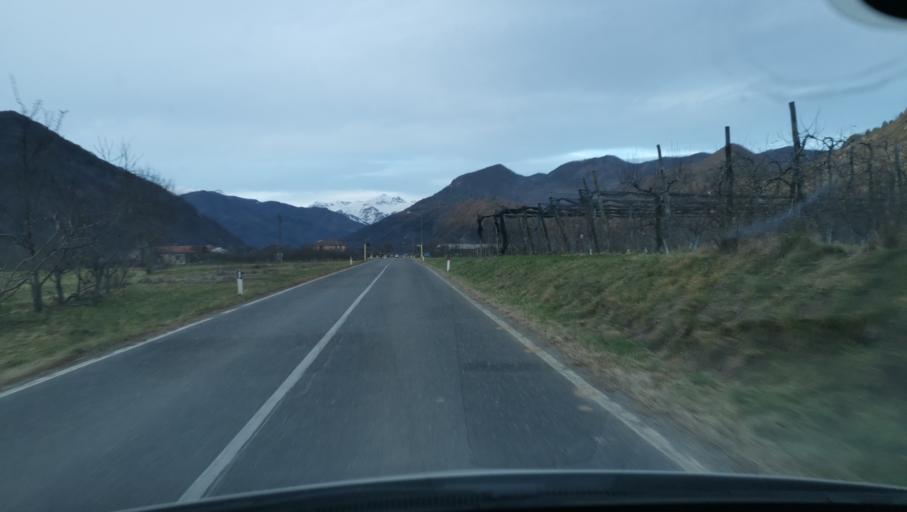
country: IT
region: Piedmont
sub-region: Provincia di Cuneo
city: Valgrana
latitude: 44.4121
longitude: 7.3705
